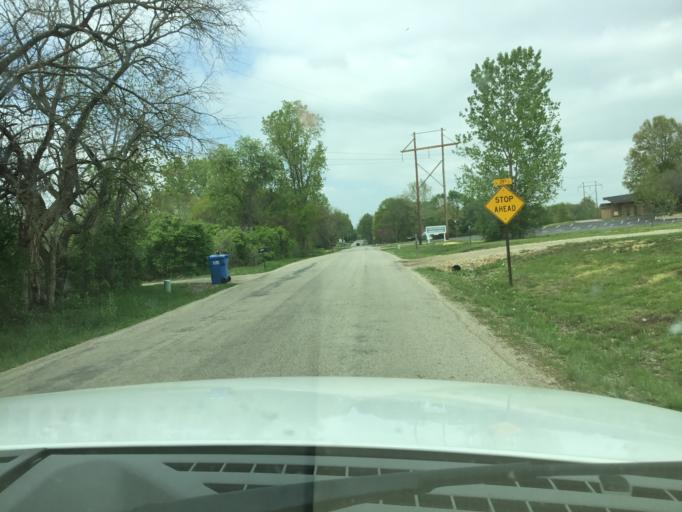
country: US
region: Kansas
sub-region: Shawnee County
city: Topeka
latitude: 39.0130
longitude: -95.5861
